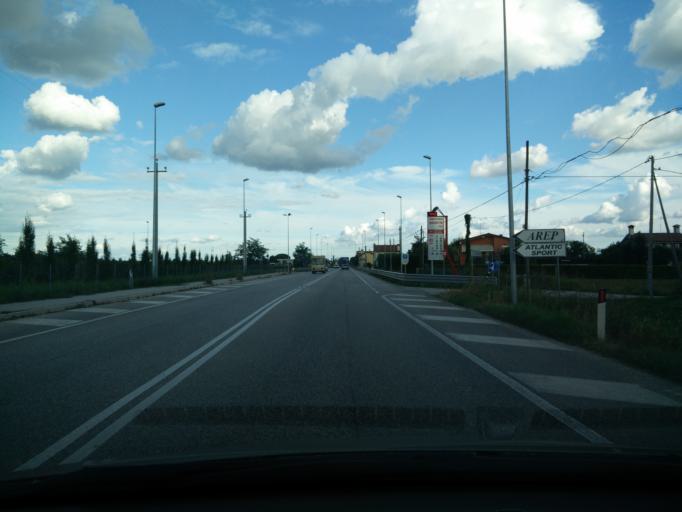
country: IT
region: Veneto
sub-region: Provincia di Treviso
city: Ponzano
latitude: 45.7310
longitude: 12.2272
